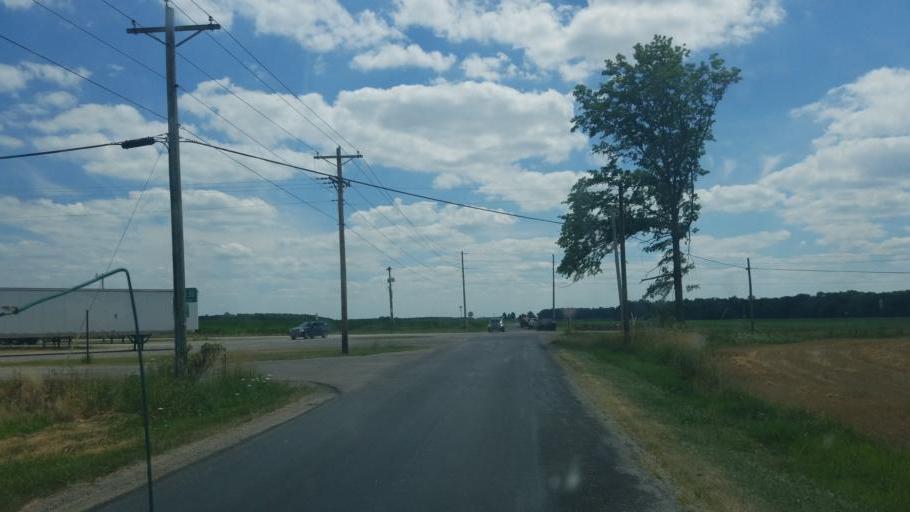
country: US
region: Ohio
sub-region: Williams County
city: Edgerton
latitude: 41.4489
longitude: -84.6911
